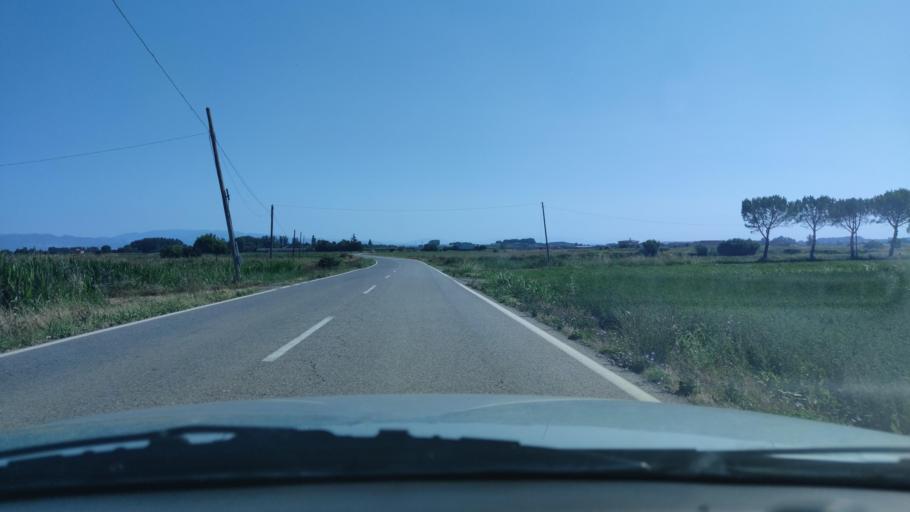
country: ES
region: Catalonia
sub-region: Provincia de Lleida
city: Bellvis
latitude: 41.6533
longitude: 0.8037
